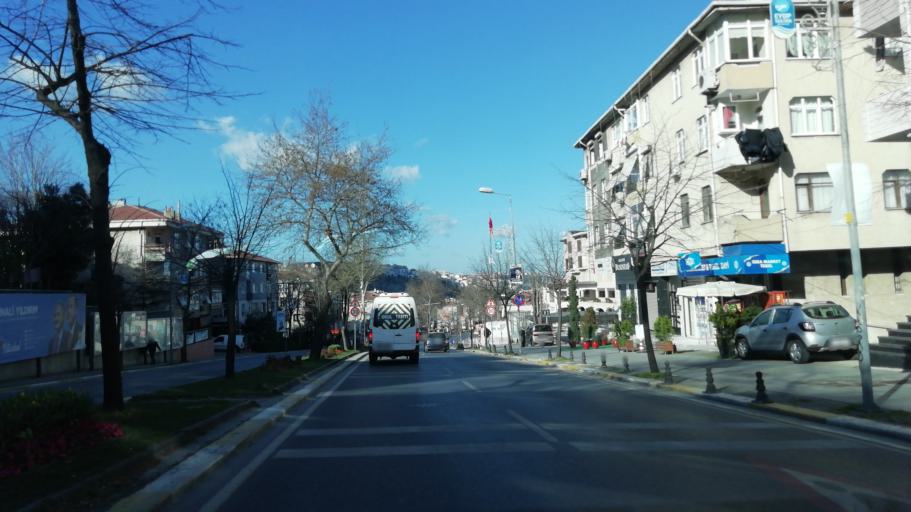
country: TR
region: Istanbul
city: Istanbul
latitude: 41.0423
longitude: 28.9284
